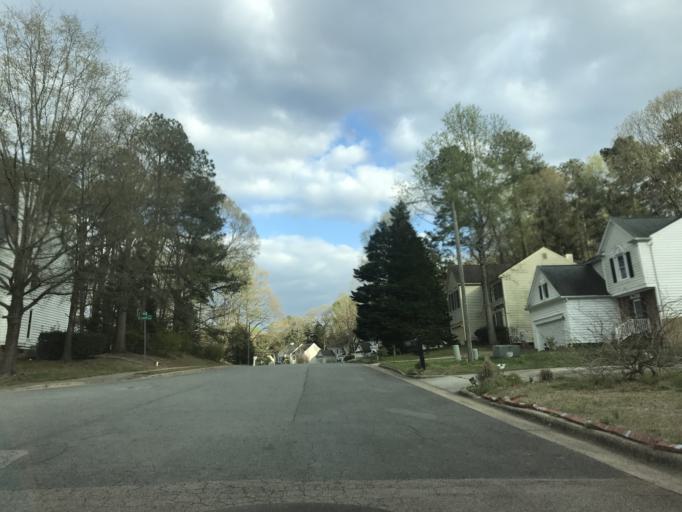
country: US
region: North Carolina
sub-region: Wake County
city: Knightdale
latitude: 35.8658
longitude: -78.5582
